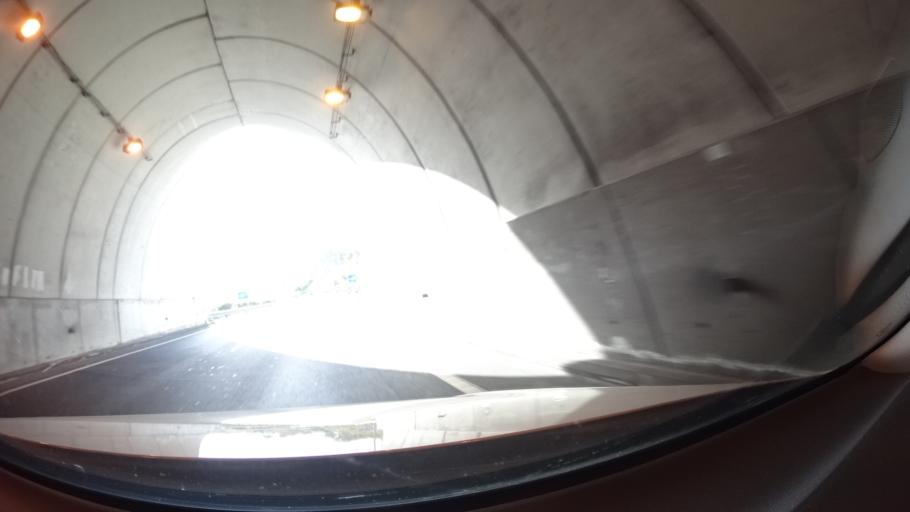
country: ES
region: Canary Islands
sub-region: Provincia de Las Palmas
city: Santa Brigida
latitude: 28.0475
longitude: -15.4693
